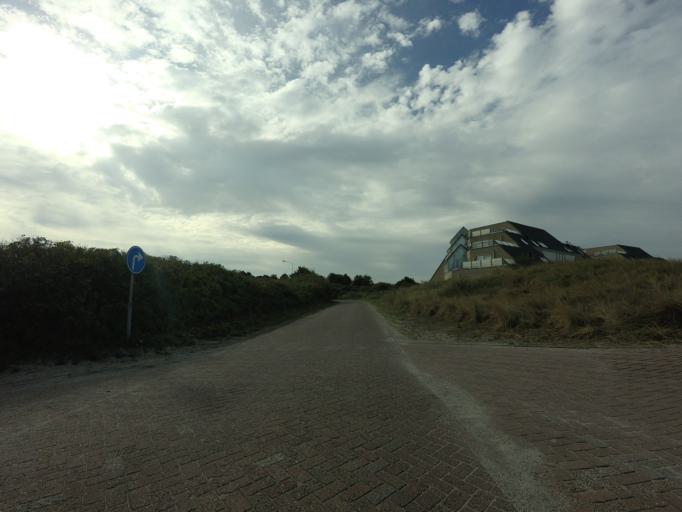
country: NL
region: Friesland
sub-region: Gemeente Ameland
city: Nes
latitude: 53.4570
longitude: 5.7752
